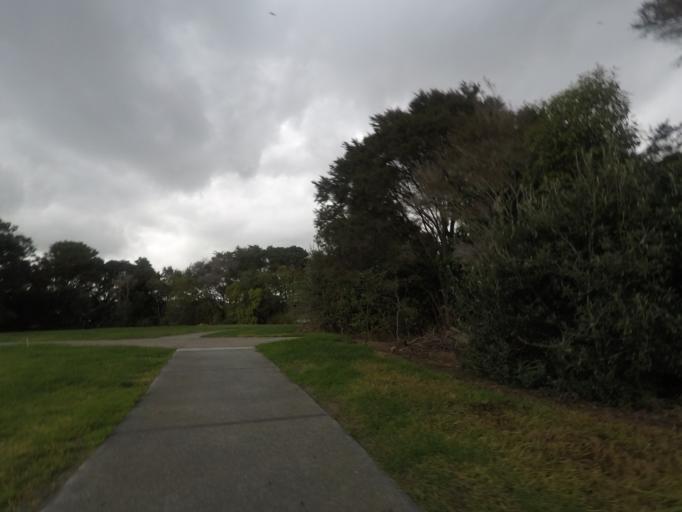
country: NZ
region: Auckland
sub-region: Auckland
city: Rosebank
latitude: -36.9011
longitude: 174.6847
